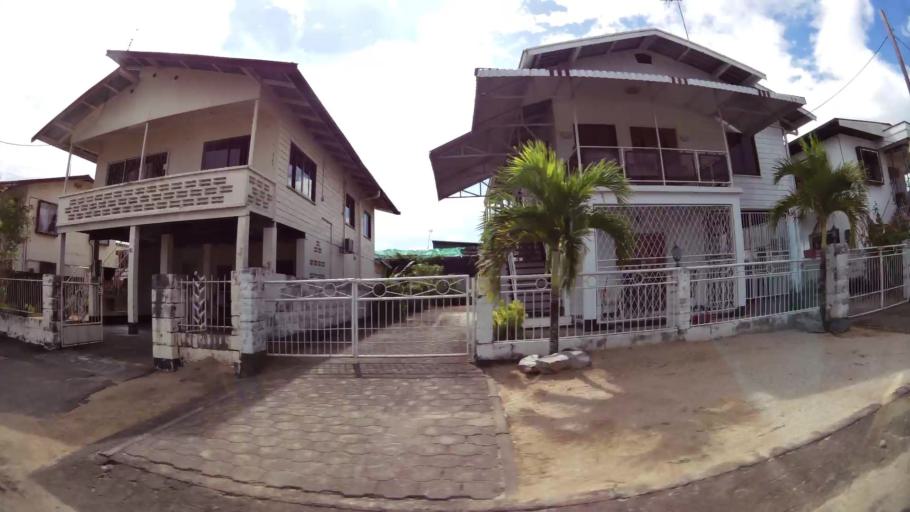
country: SR
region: Paramaribo
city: Paramaribo
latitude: 5.8426
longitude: -55.1471
